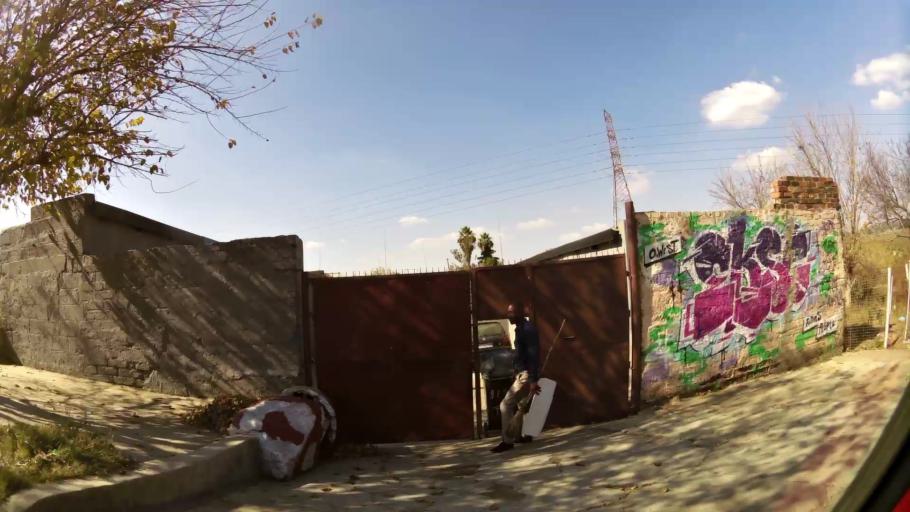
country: ZA
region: Gauteng
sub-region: City of Johannesburg Metropolitan Municipality
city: Soweto
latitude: -26.2446
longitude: 27.9069
